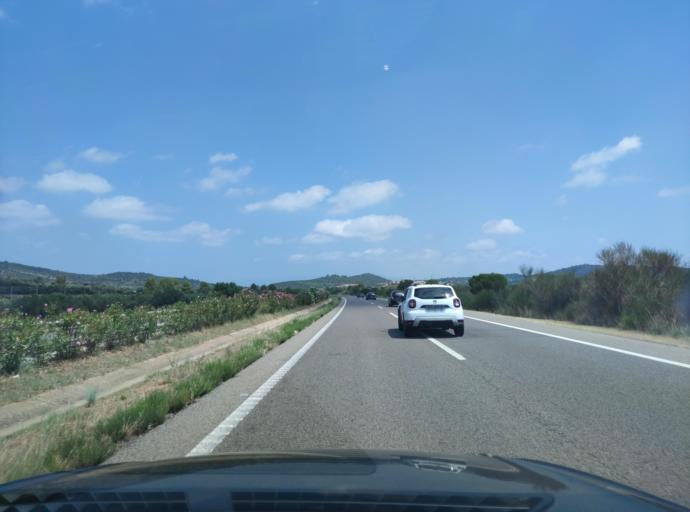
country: ES
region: Catalonia
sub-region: Provincia de Tarragona
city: Santa Barbara
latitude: 40.6526
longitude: 0.5088
